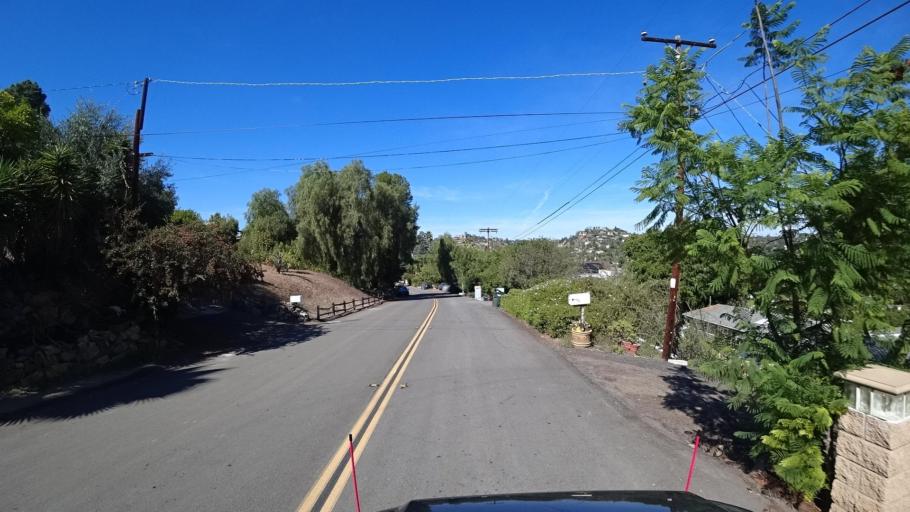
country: US
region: California
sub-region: San Diego County
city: Casa de Oro-Mount Helix
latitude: 32.7487
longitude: -116.9672
